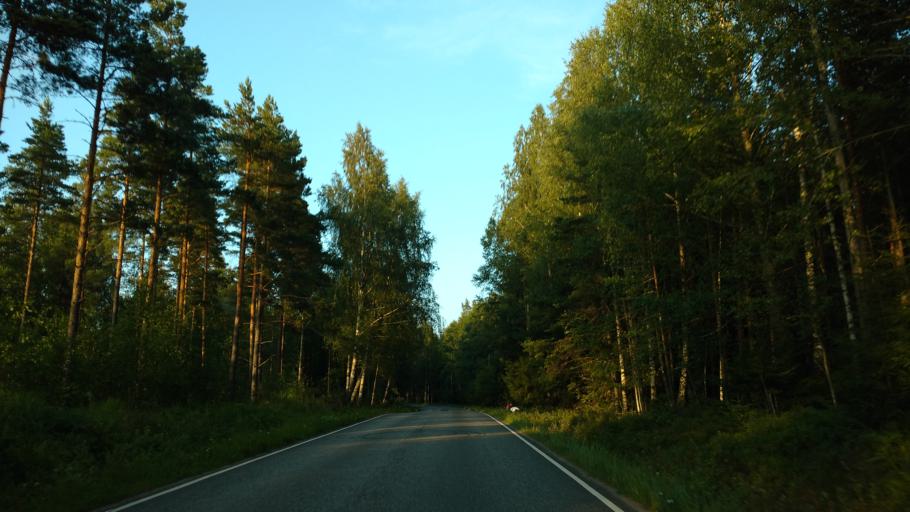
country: FI
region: Varsinais-Suomi
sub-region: Salo
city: Saerkisalo
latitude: 60.2290
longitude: 22.9279
